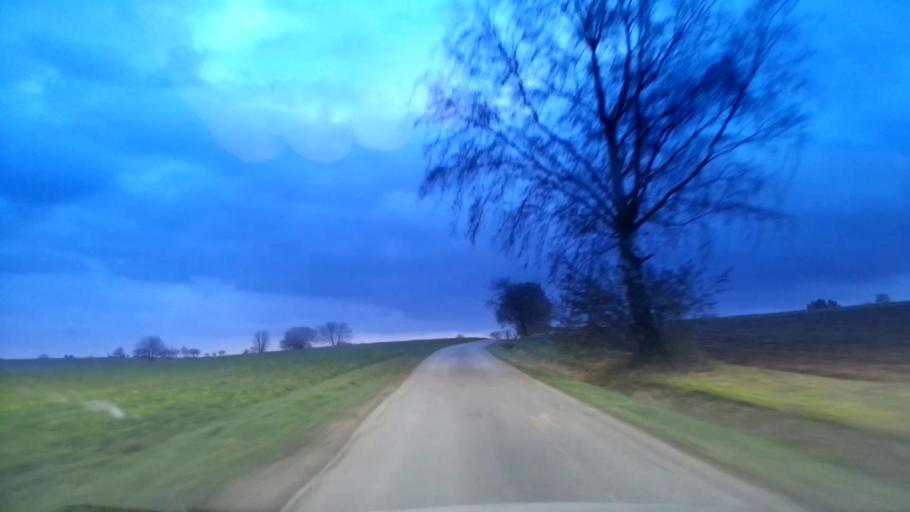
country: DE
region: Bavaria
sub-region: Upper Palatinate
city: Fuchsmuhl
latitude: 49.9218
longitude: 12.1628
